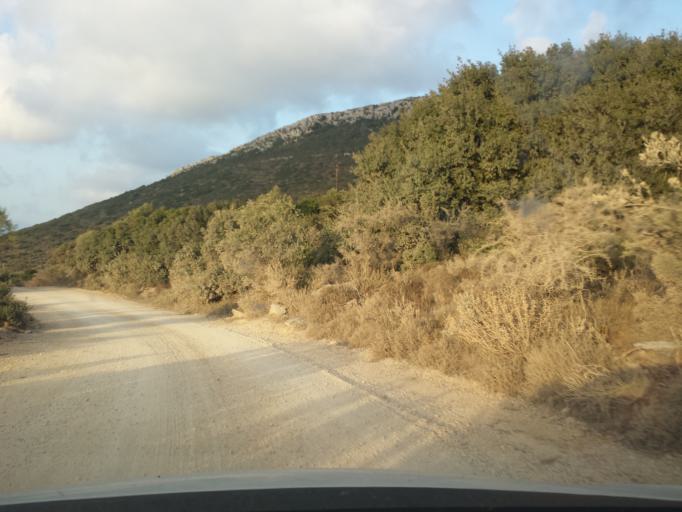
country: GR
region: Peloponnese
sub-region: Nomos Messinias
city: Pylos
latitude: 36.8919
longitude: 21.6894
